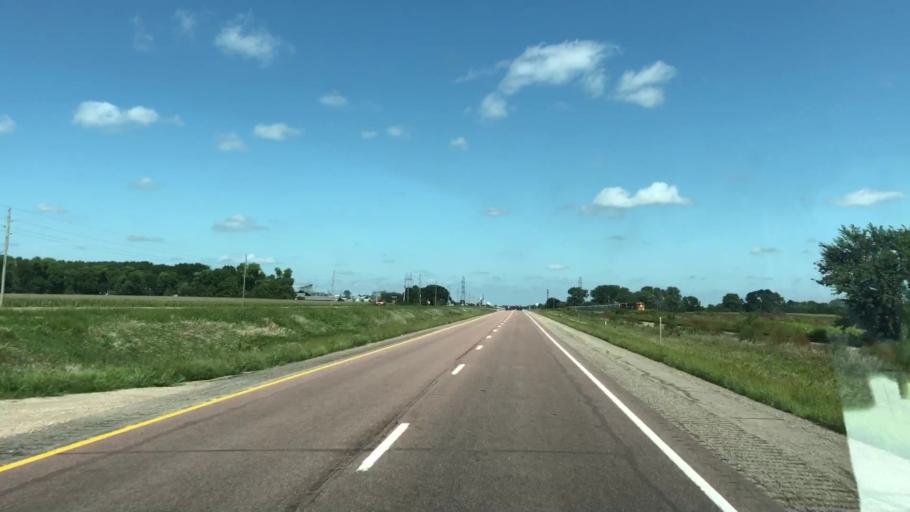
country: US
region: Iowa
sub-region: Woodbury County
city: Sioux City
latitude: 42.5903
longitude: -96.3067
